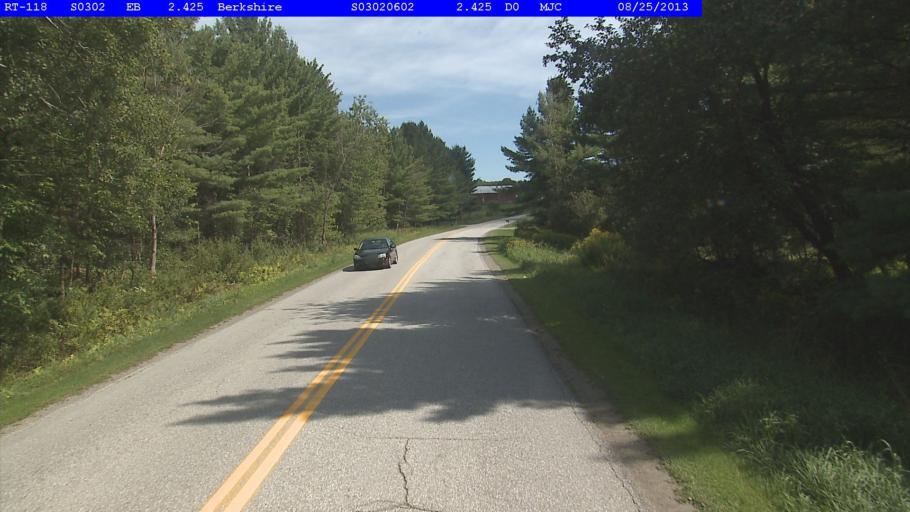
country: US
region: Vermont
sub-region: Franklin County
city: Enosburg Falls
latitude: 44.9753
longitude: -72.7693
